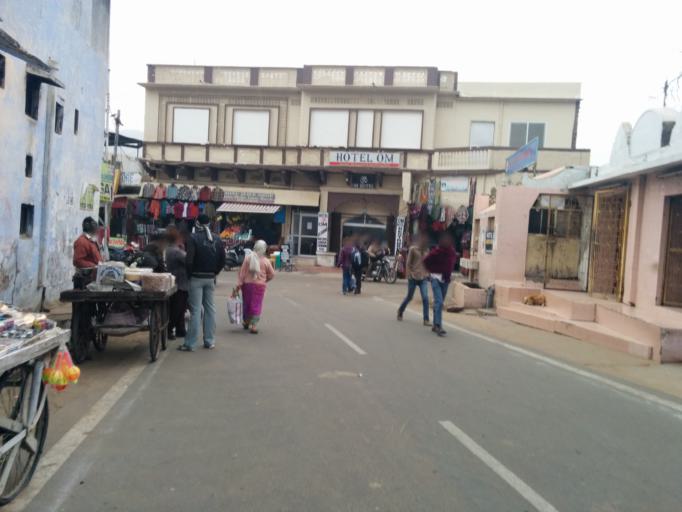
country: IN
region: Rajasthan
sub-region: Ajmer
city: Pushkar
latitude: 26.4879
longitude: 74.5581
